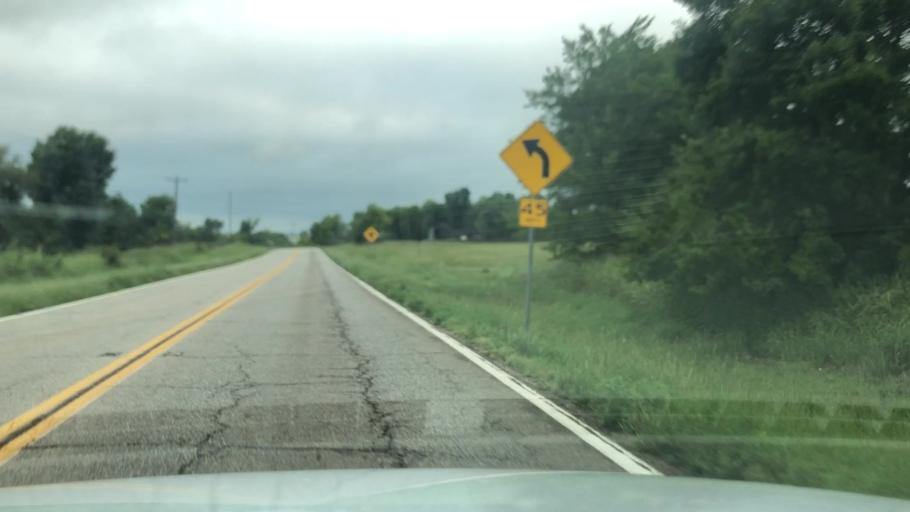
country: US
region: Oklahoma
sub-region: Nowata County
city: Nowata
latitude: 36.7118
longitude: -95.6610
